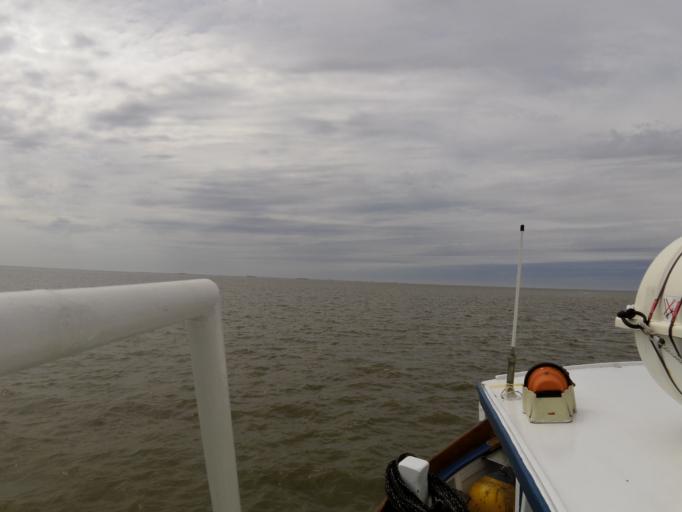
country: DE
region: Schleswig-Holstein
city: Langeness
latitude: 54.6149
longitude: 8.6343
